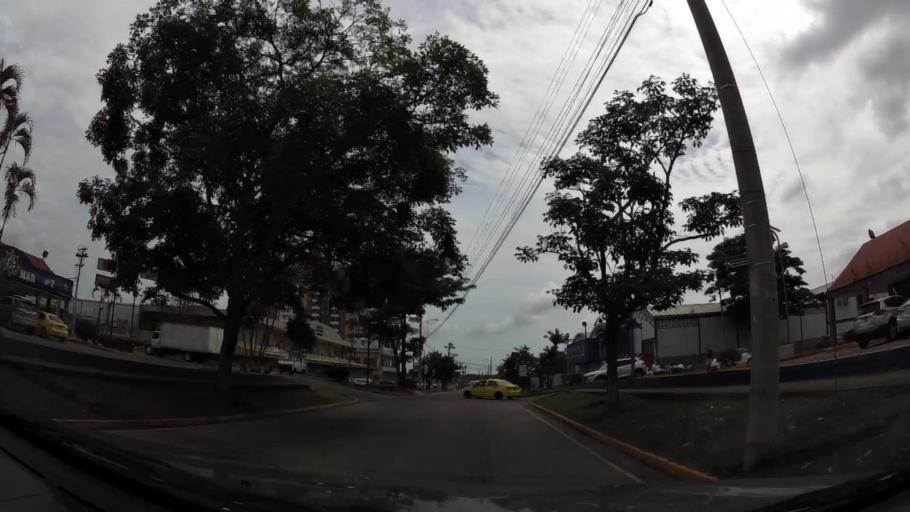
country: PA
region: Panama
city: San Miguelito
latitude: 9.0603
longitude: -79.4227
